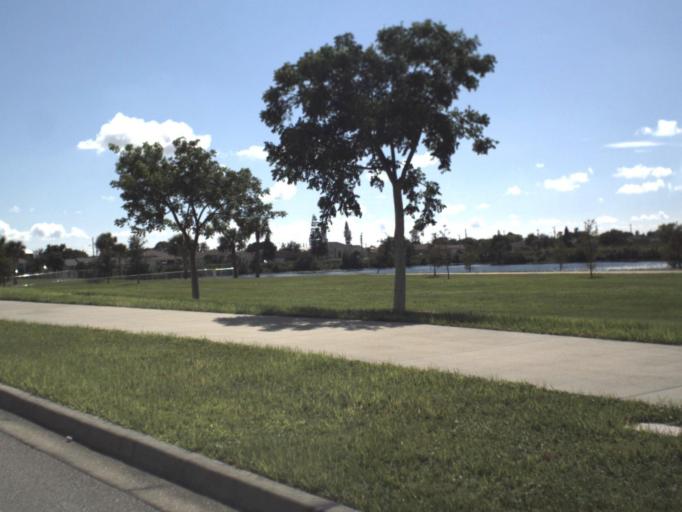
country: US
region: Florida
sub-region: Lee County
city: Lochmoor Waterway Estates
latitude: 26.6759
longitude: -81.9417
